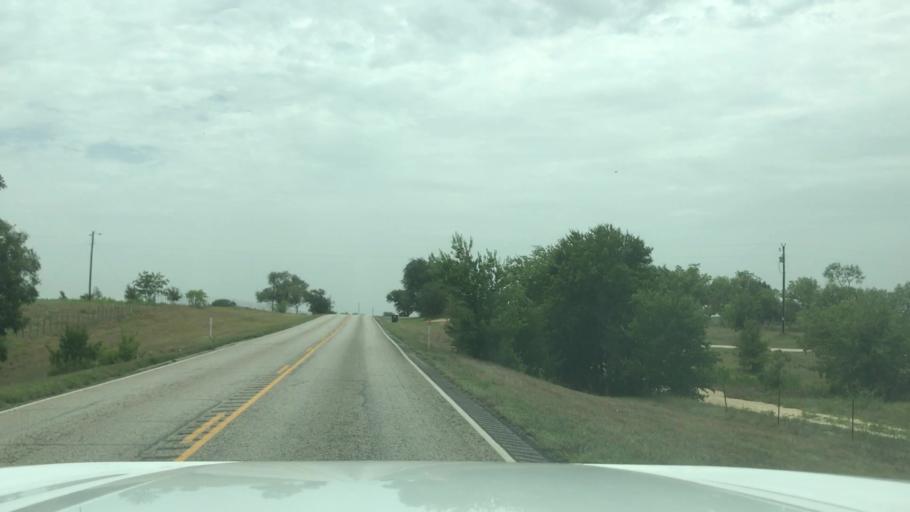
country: US
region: Texas
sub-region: Hamilton County
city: Hico
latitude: 32.0454
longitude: -98.1434
